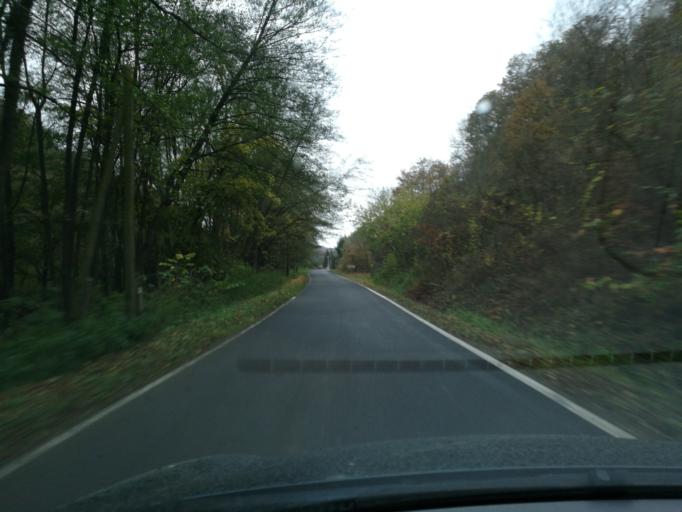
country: HU
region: Nograd
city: Paszto
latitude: 47.9681
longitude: 19.6176
